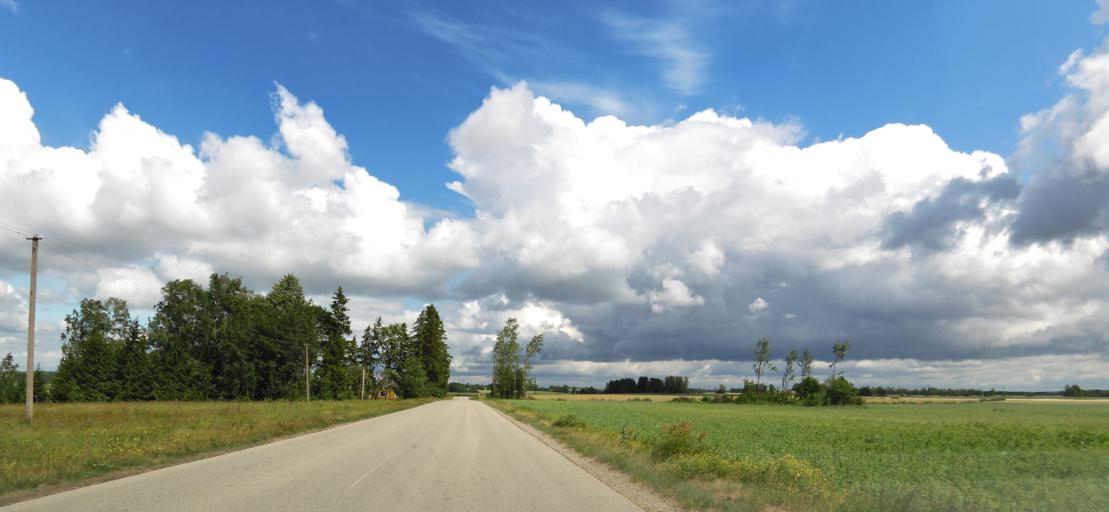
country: LT
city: Vabalninkas
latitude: 55.8906
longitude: 24.7976
